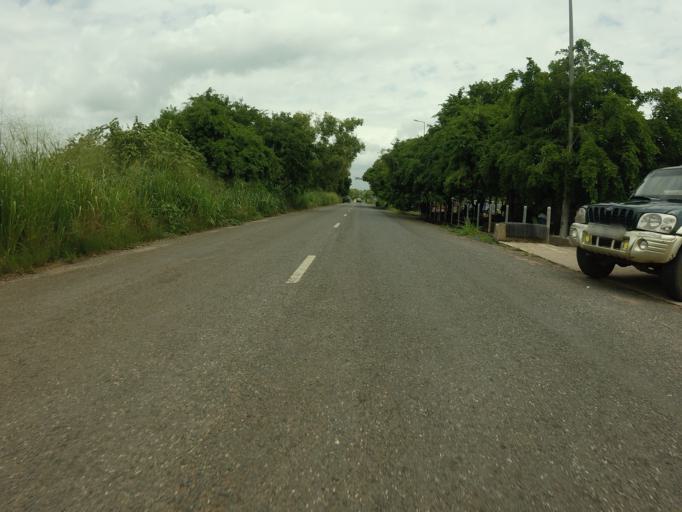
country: GH
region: Volta
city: Ho
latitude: 6.5897
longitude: 0.4627
